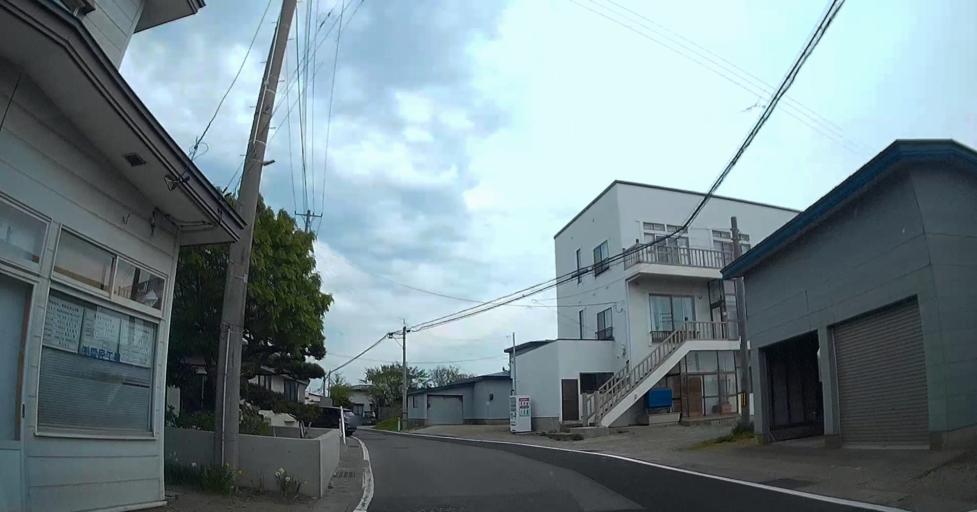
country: JP
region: Aomori
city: Shimokizukuri
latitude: 41.0349
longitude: 140.3296
